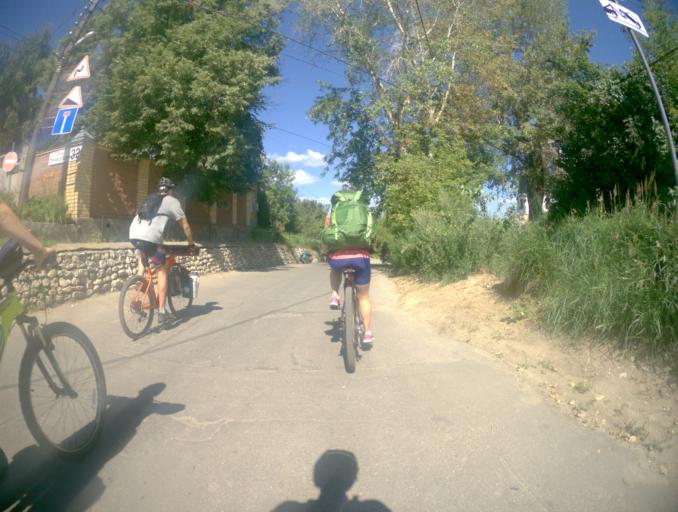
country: RU
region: Nizjnij Novgorod
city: Nizhniy Novgorod
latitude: 56.3226
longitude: 44.0430
